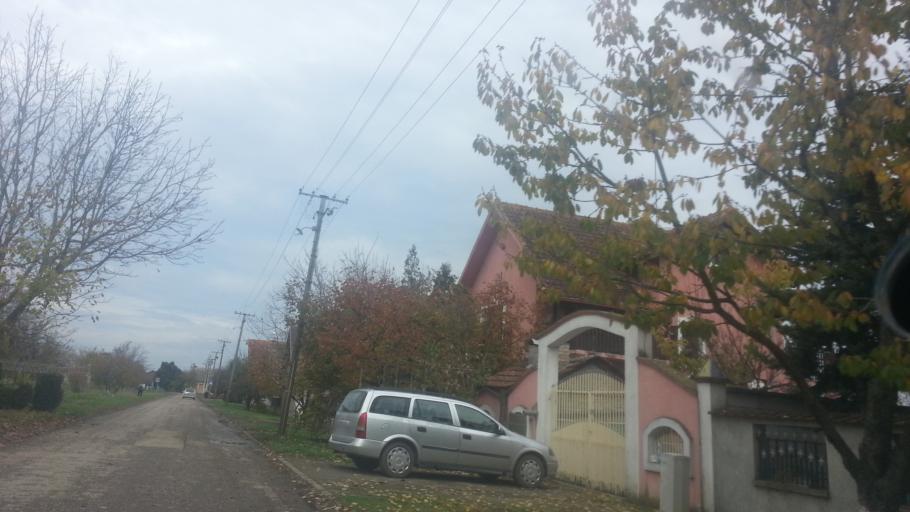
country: RS
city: Golubinci
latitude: 44.9843
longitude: 20.0804
